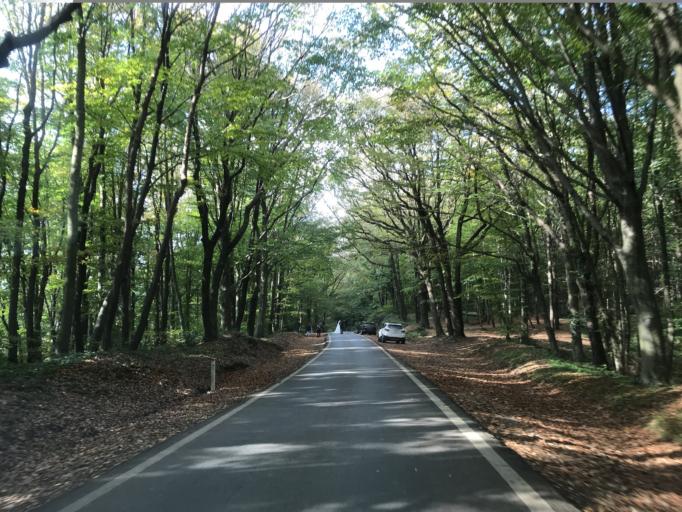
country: TR
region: Istanbul
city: Arikoey
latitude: 41.1863
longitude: 28.9861
